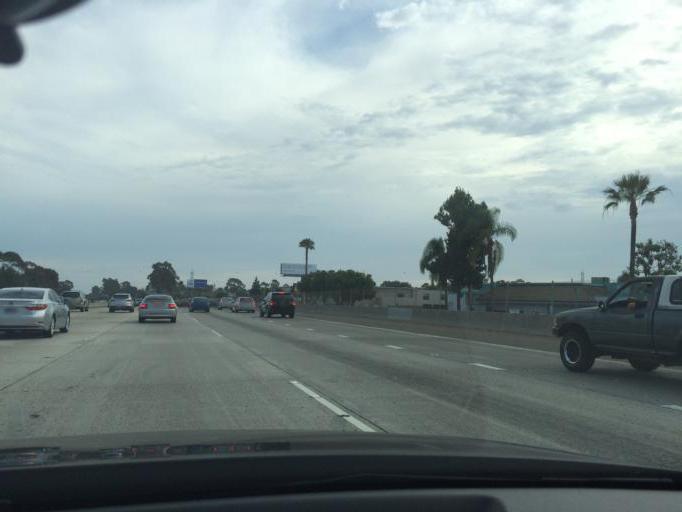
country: US
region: California
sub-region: San Diego County
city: San Diego
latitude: 32.8161
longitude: -117.1499
